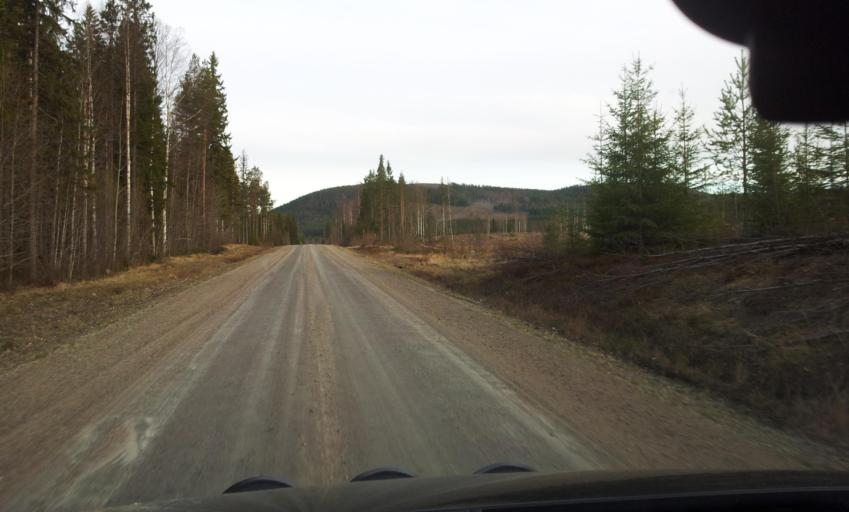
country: SE
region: Gaevleborg
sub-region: Ljusdals Kommun
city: Farila
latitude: 62.0768
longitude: 15.7756
